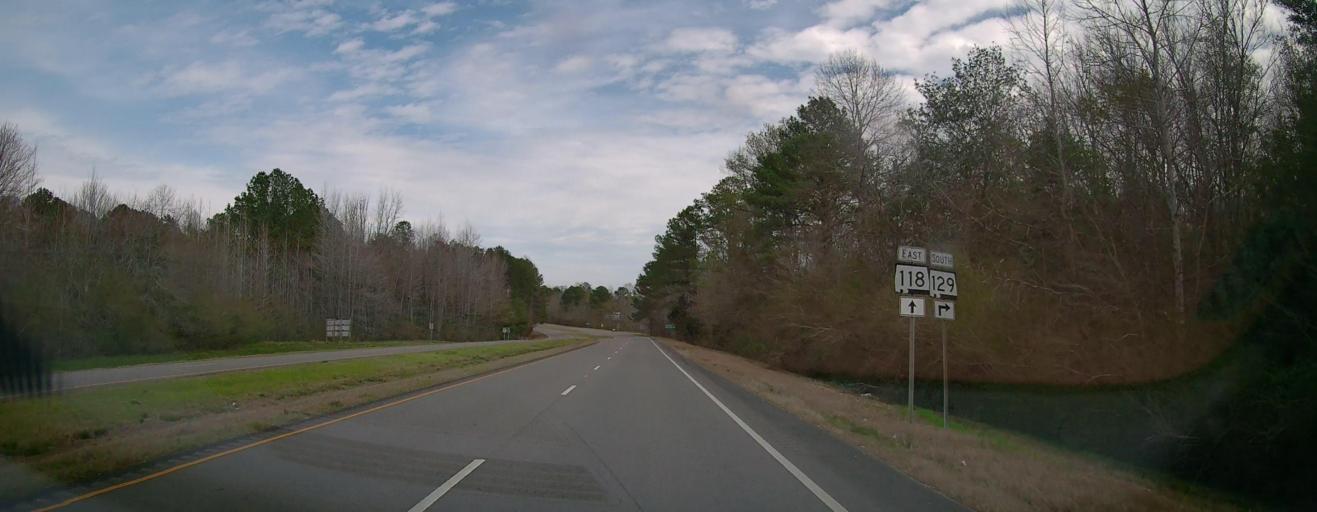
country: US
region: Alabama
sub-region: Marion County
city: Winfield
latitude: 33.9287
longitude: -87.7628
